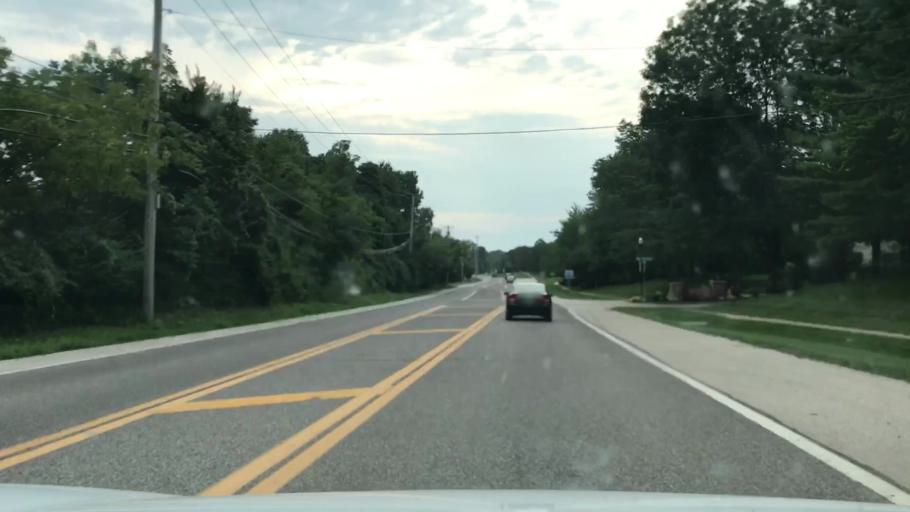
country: US
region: Missouri
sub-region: Saint Louis County
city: Chesterfield
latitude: 38.6557
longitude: -90.6092
